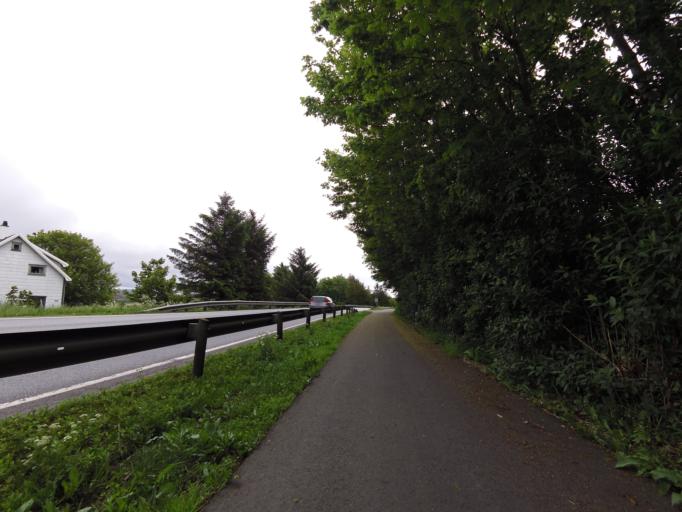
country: NO
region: Rogaland
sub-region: Klepp
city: Kleppe
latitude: 58.8192
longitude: 5.5897
